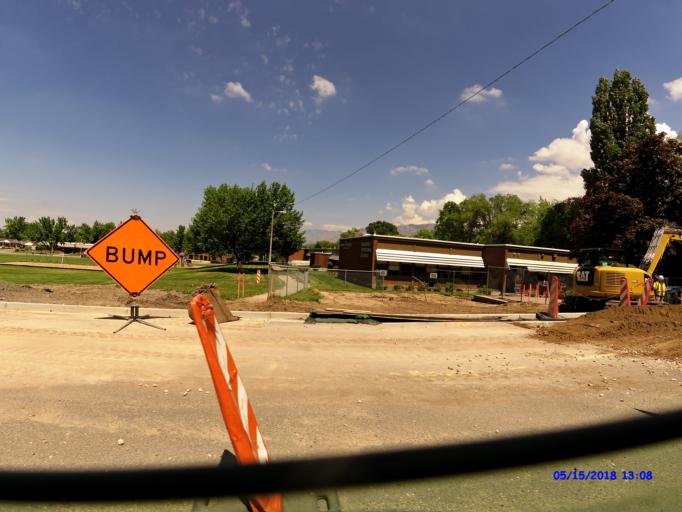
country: US
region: Utah
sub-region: Weber County
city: South Ogden
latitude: 41.1905
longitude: -111.9655
